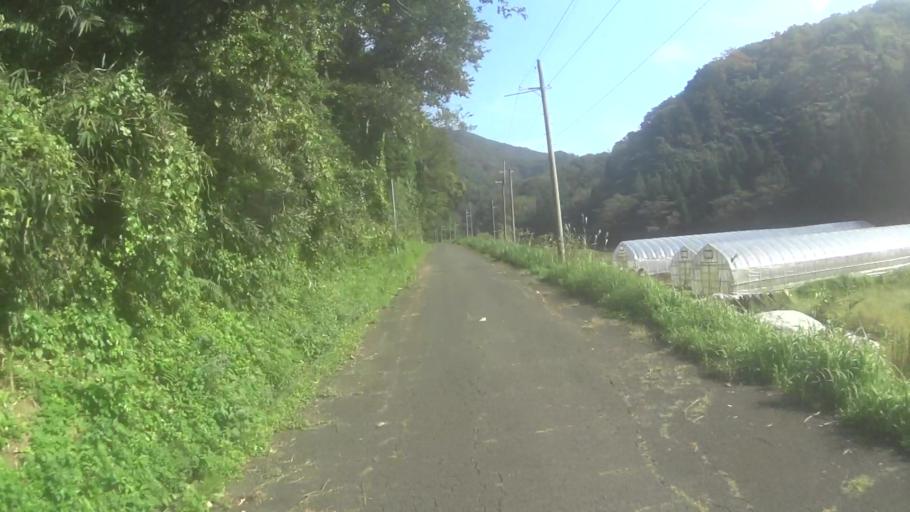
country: JP
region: Kyoto
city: Miyazu
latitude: 35.7160
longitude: 135.1238
